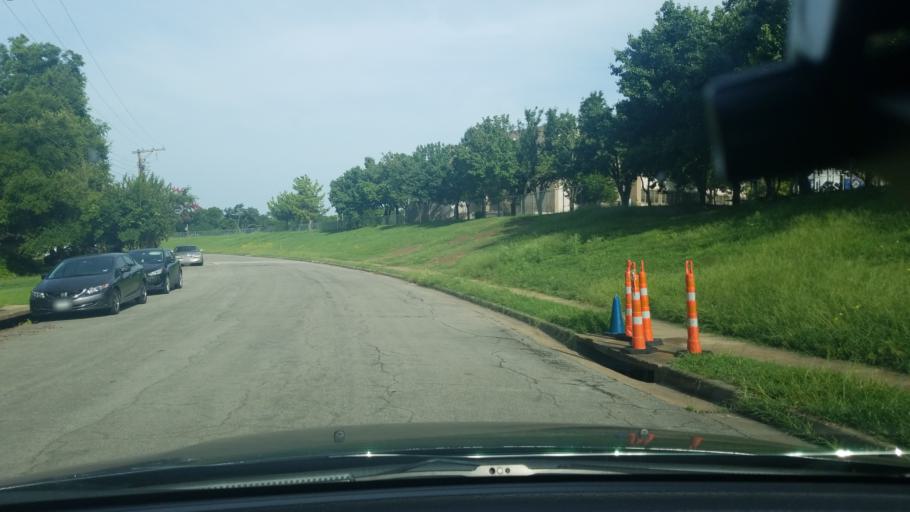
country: US
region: Texas
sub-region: Dallas County
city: Highland Park
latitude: 32.8003
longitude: -96.7059
